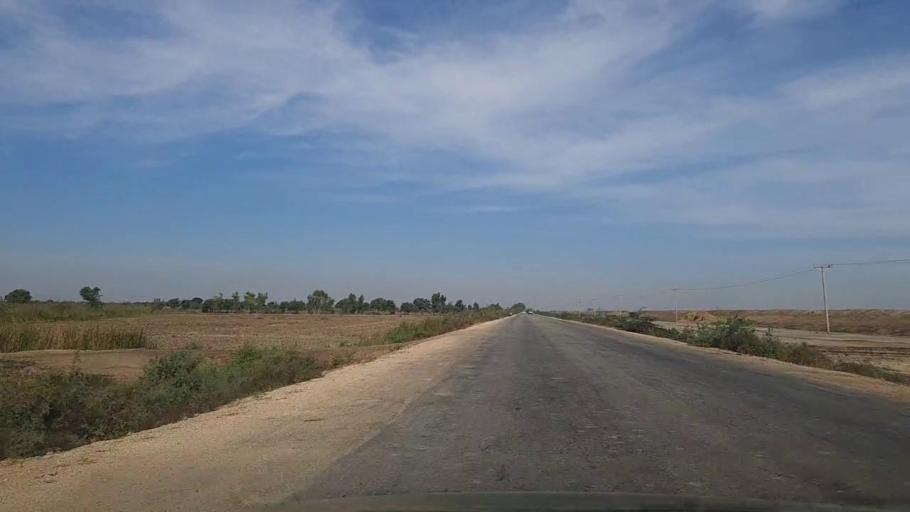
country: PK
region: Sindh
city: Daro Mehar
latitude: 24.9478
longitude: 68.1120
